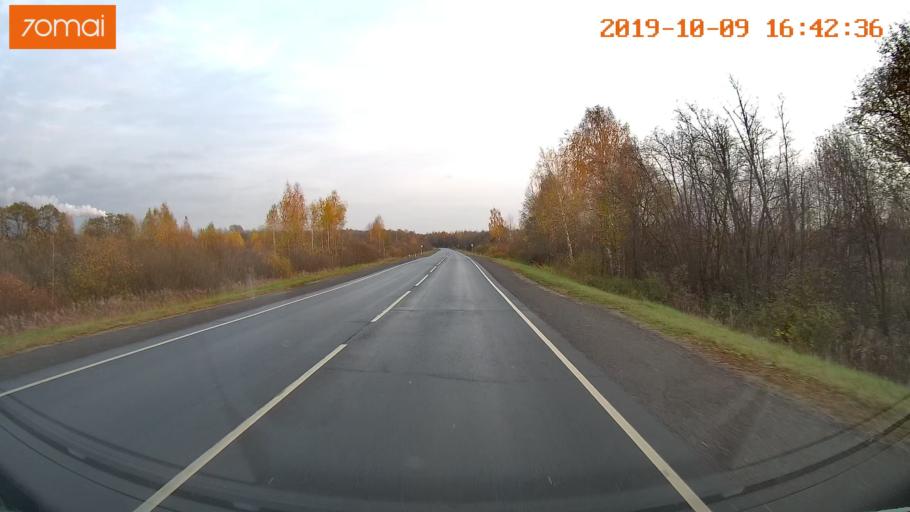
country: RU
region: Kostroma
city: Volgorechensk
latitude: 57.4603
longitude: 41.1037
